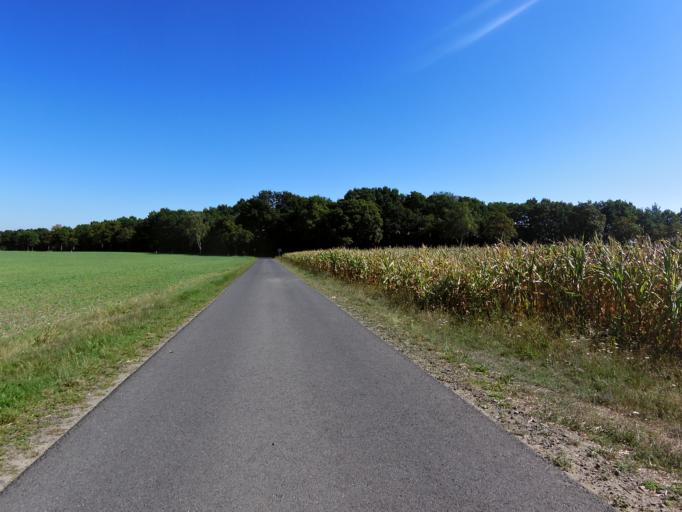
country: DE
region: Saxony-Anhalt
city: Pretzsch
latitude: 51.6801
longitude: 12.8252
